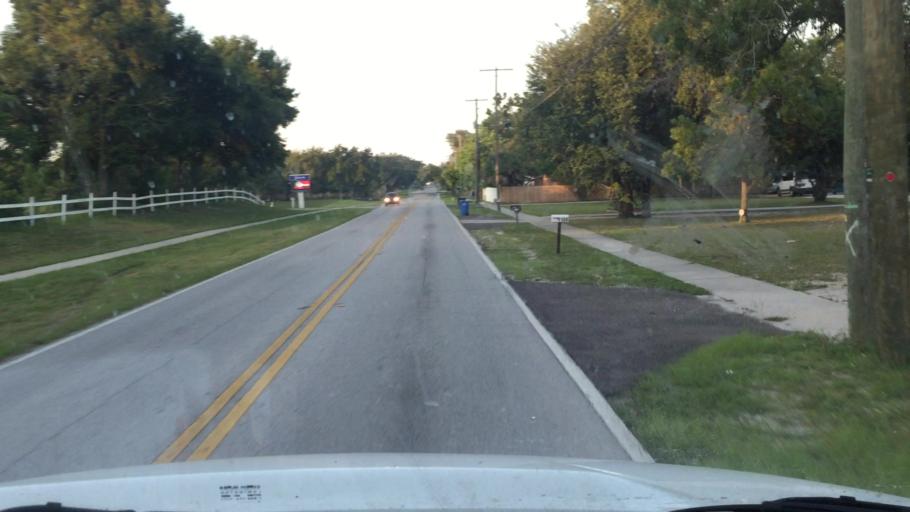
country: US
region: Florida
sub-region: Hillsborough County
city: Brandon
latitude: 27.9569
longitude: -82.2777
